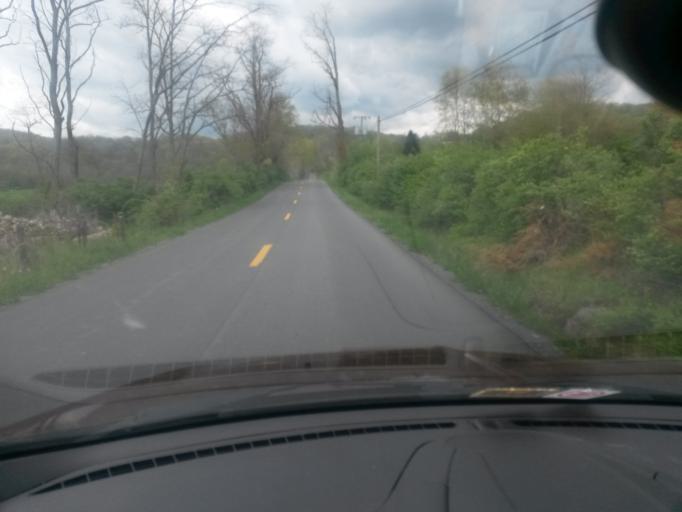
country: US
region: West Virginia
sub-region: Greenbrier County
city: Lewisburg
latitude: 37.9338
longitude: -80.4009
